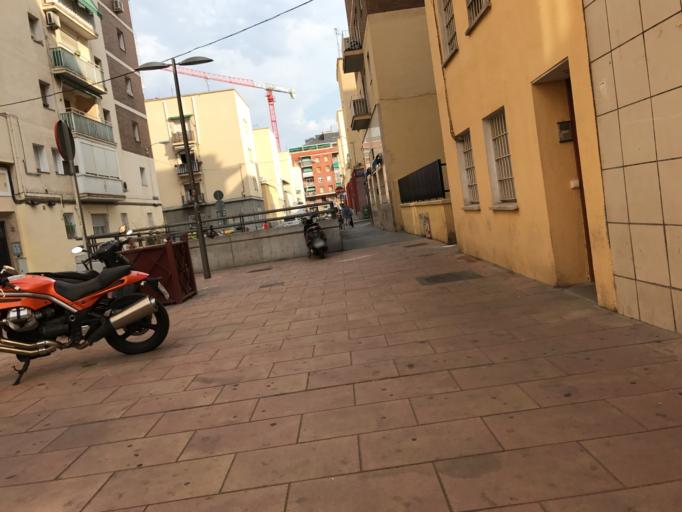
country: ES
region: Madrid
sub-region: Provincia de Madrid
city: Salamanca
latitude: 40.4387
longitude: -3.6766
